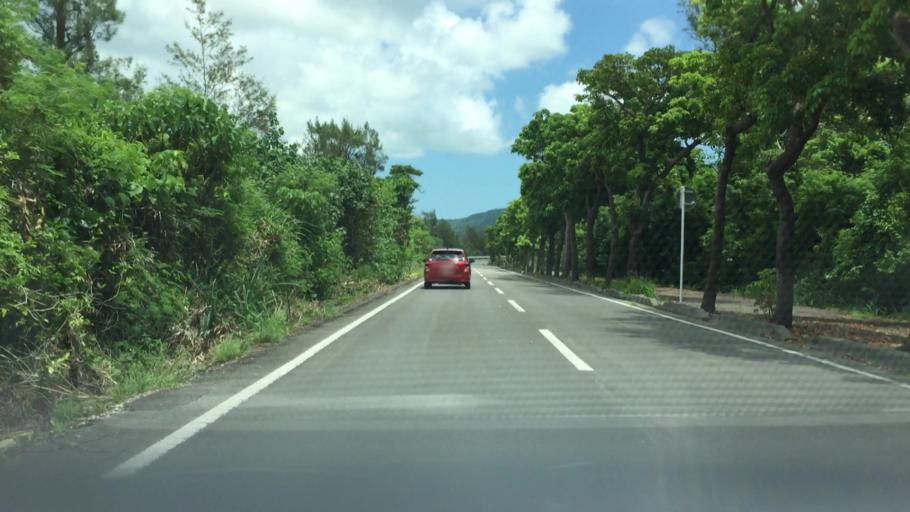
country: JP
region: Okinawa
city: Ishigaki
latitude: 24.3984
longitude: 124.1407
